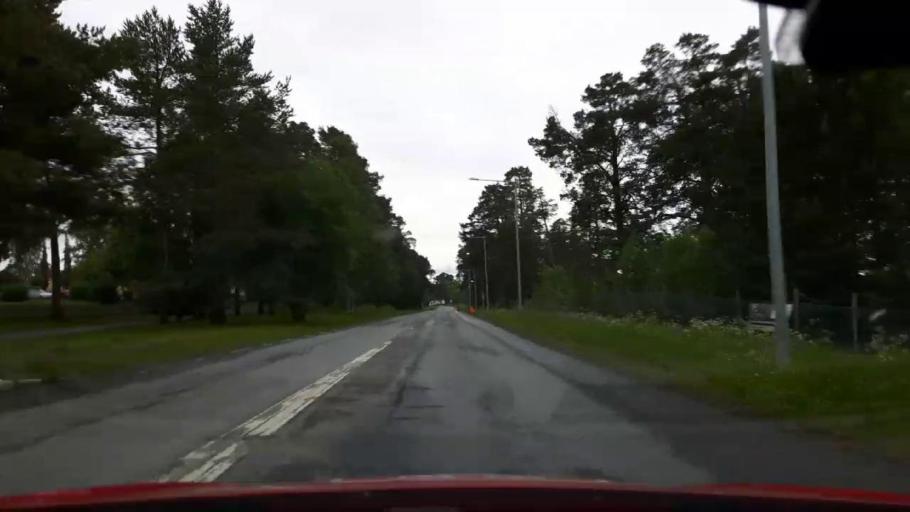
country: SE
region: Jaemtland
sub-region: OEstersunds Kommun
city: Ostersund
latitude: 63.1867
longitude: 14.6503
